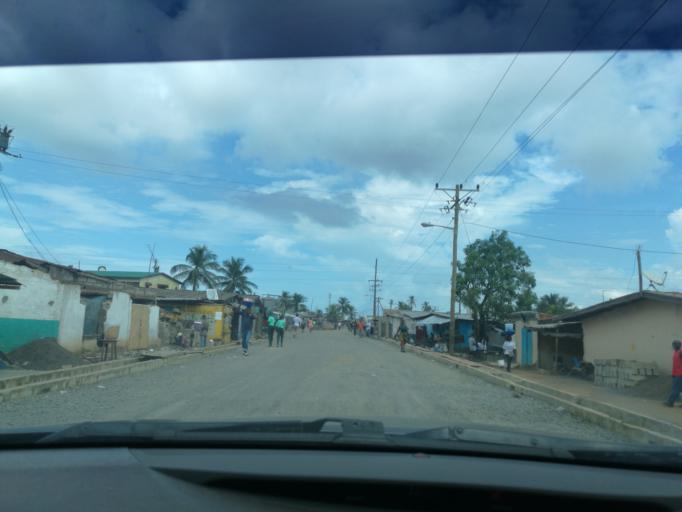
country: LR
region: Montserrado
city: Monrovia
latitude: 6.3351
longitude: -10.7850
